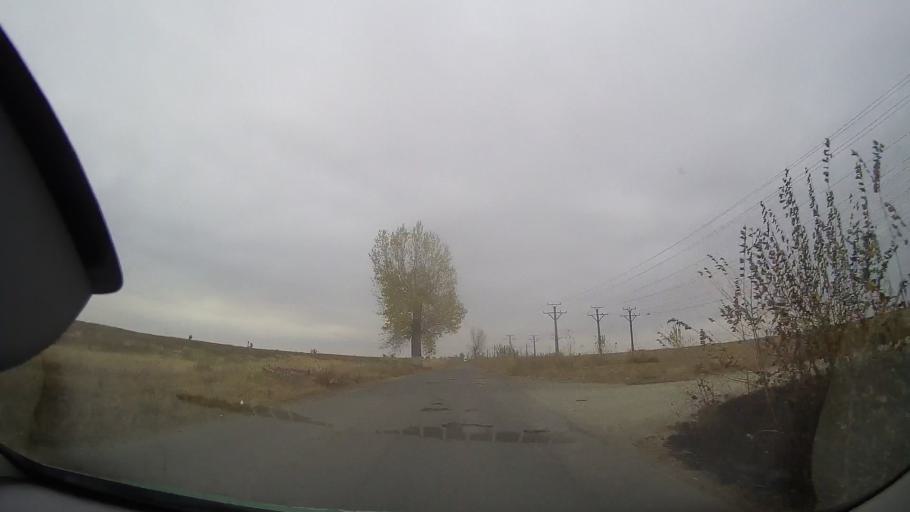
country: RO
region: Braila
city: Dudesti
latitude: 44.9130
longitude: 27.4303
